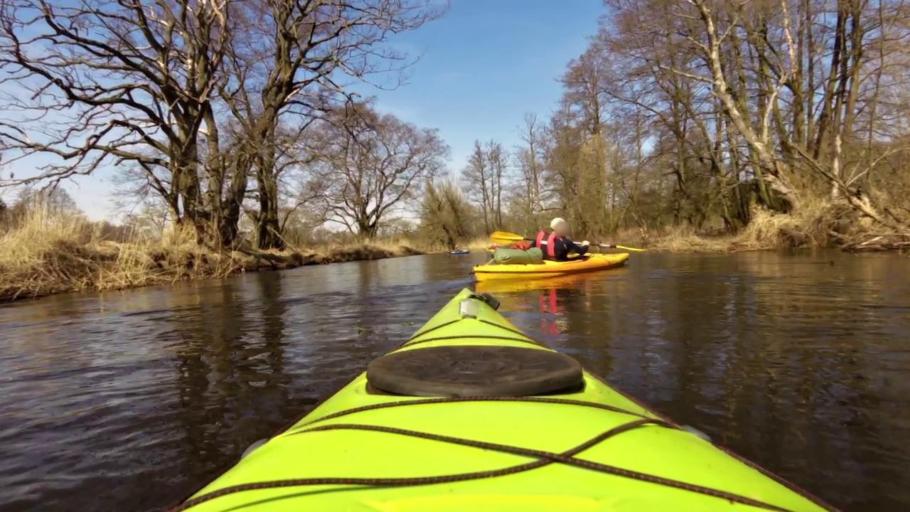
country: PL
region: West Pomeranian Voivodeship
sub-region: Powiat lobeski
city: Lobez
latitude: 53.6636
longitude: 15.5648
